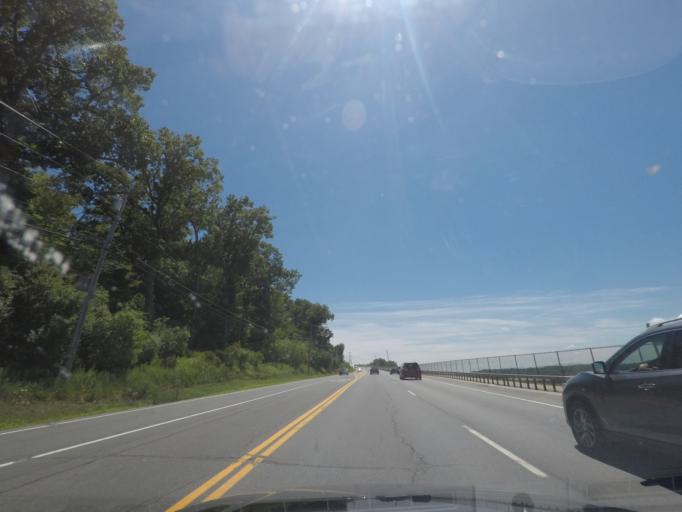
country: US
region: New York
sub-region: Rensselaer County
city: Hampton Manor
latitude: 42.6384
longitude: -73.7002
